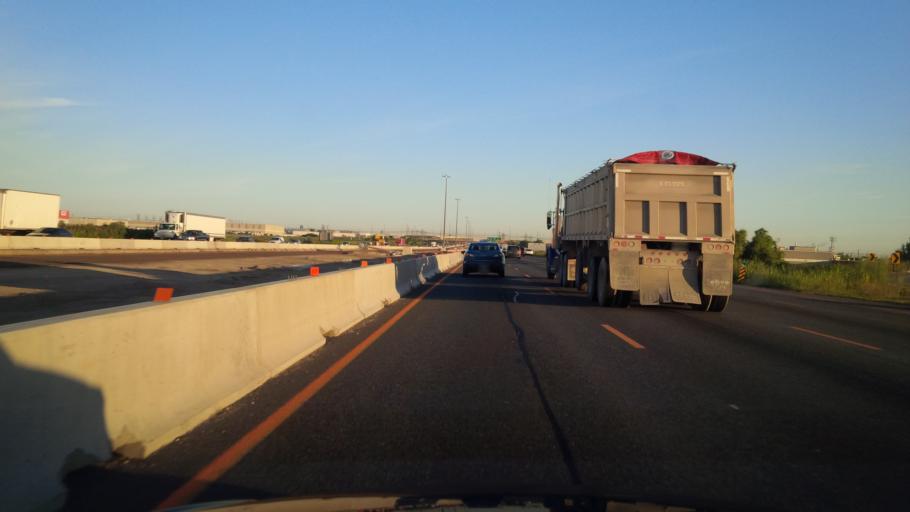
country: CA
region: Ontario
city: Mississauga
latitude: 43.6527
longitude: -79.6782
